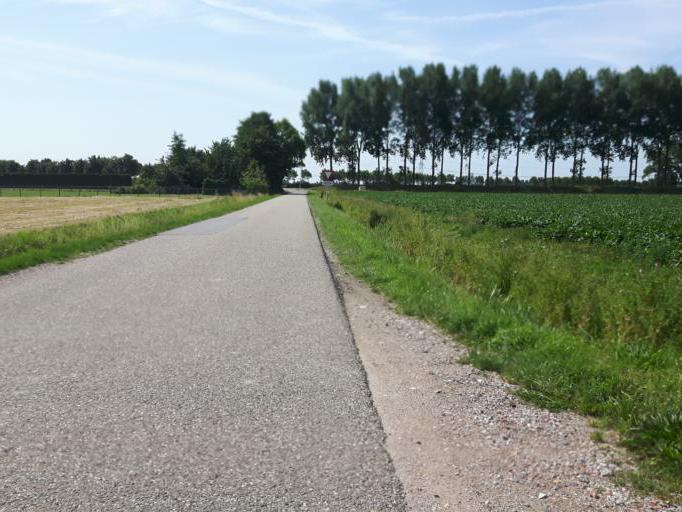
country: NL
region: Zeeland
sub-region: Gemeente Borsele
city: Borssele
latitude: 51.4427
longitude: 3.7867
